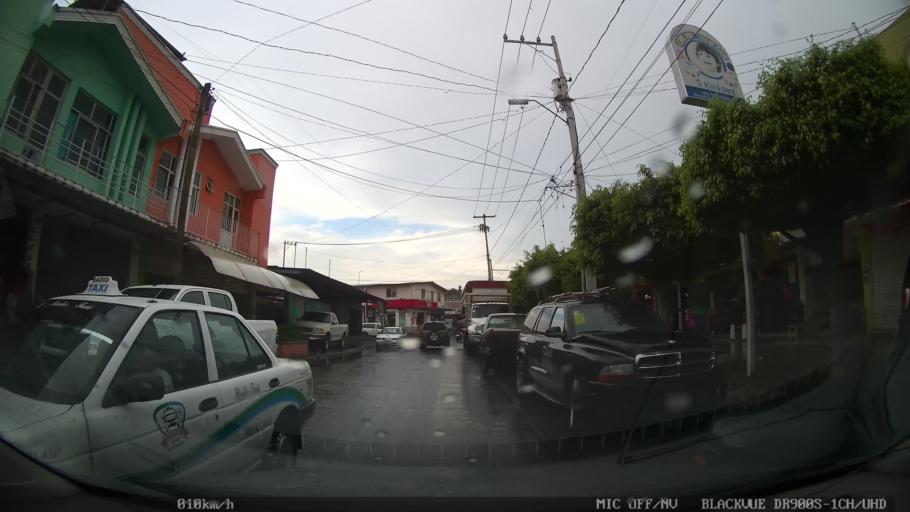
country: MX
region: Michoacan
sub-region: Uruapan
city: Santa Rosa (Santa Barbara)
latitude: 19.4051
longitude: -102.0253
